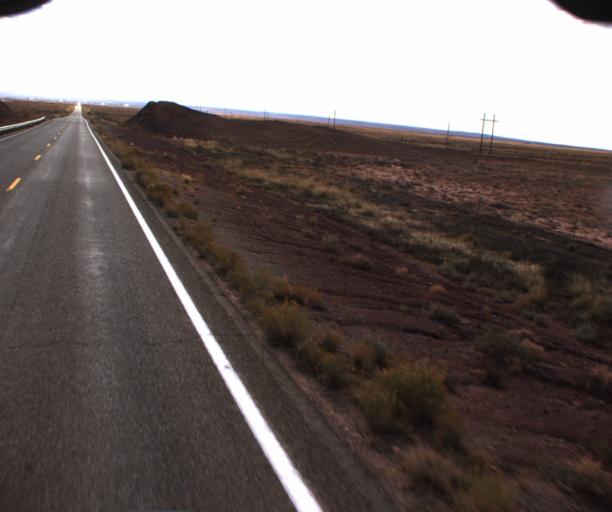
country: US
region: Arizona
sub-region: Apache County
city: Many Farms
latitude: 36.5385
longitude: -109.5195
